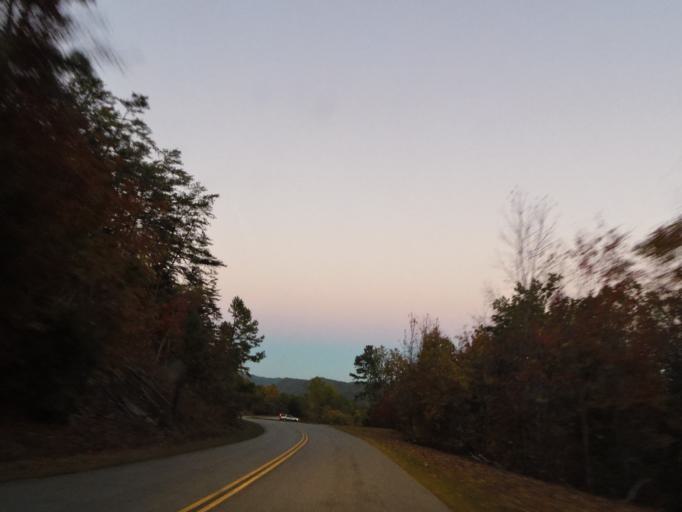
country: US
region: Tennessee
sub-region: Blount County
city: Wildwood
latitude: 35.7130
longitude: -83.8461
